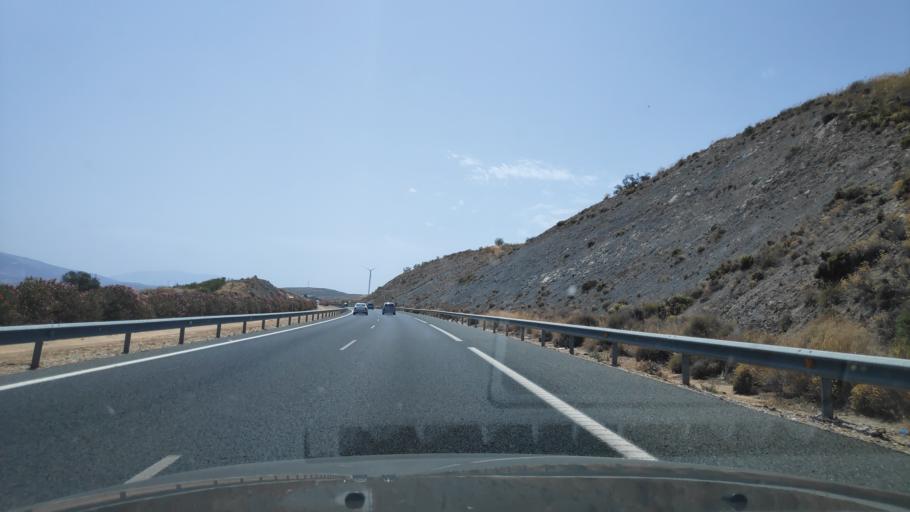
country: ES
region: Andalusia
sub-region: Provincia de Granada
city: Padul
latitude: 37.0227
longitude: -3.6441
